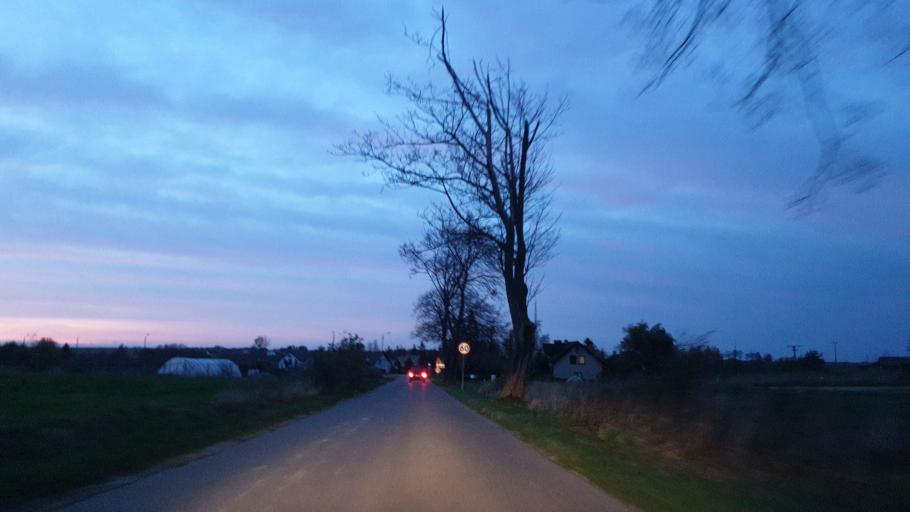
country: PL
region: Pomeranian Voivodeship
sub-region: Powiat pucki
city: Krokowa
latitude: 54.7824
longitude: 18.2005
